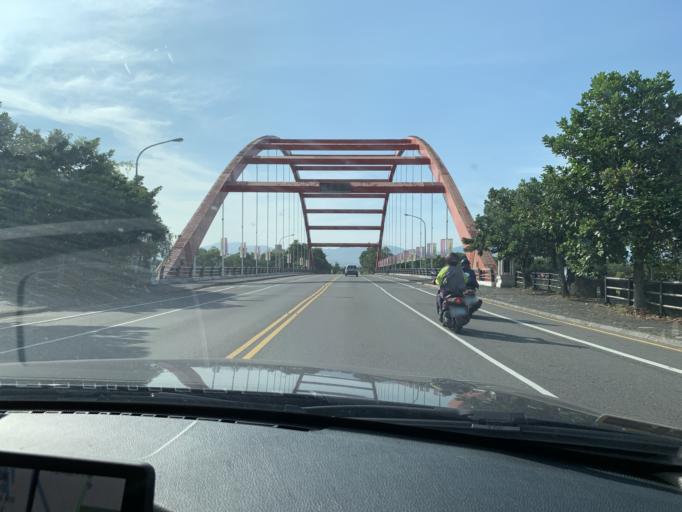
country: TW
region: Taiwan
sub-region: Yilan
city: Yilan
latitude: 24.6690
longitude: 121.8148
